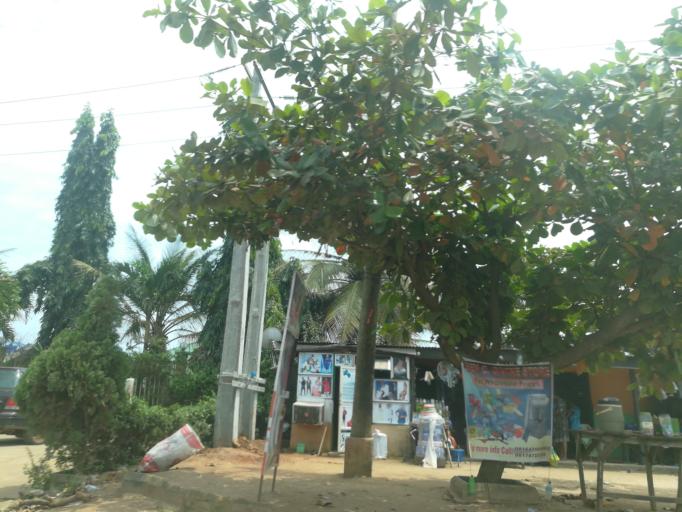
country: NG
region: Lagos
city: Ikorodu
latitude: 6.6077
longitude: 3.5910
